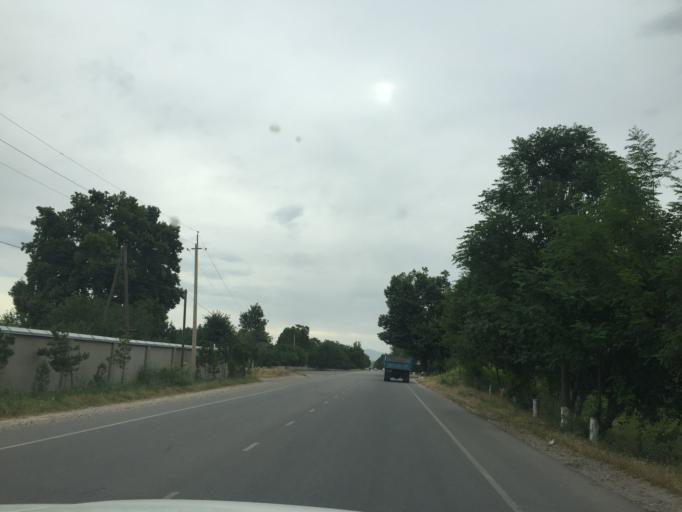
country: TJ
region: Republican Subordination
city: Vahdat
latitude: 38.5097
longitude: 69.0487
